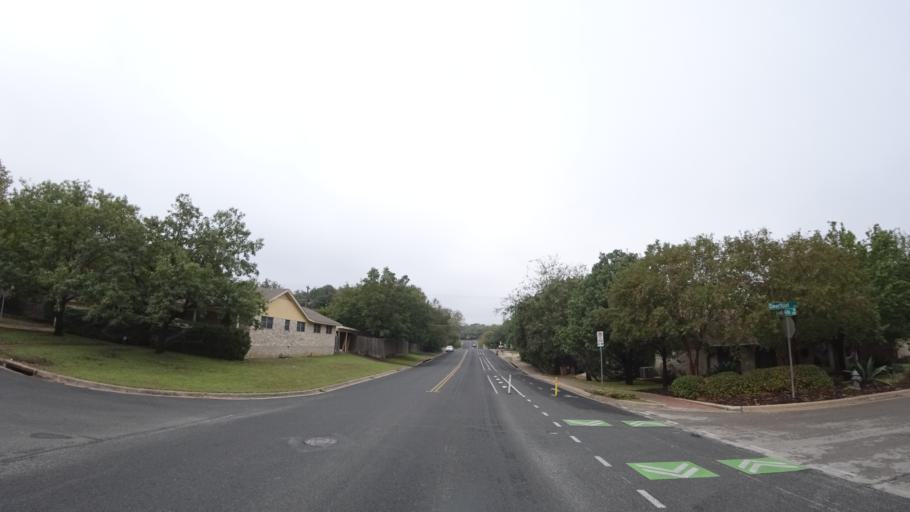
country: US
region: Texas
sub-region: Travis County
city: Rollingwood
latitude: 30.2590
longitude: -97.7791
